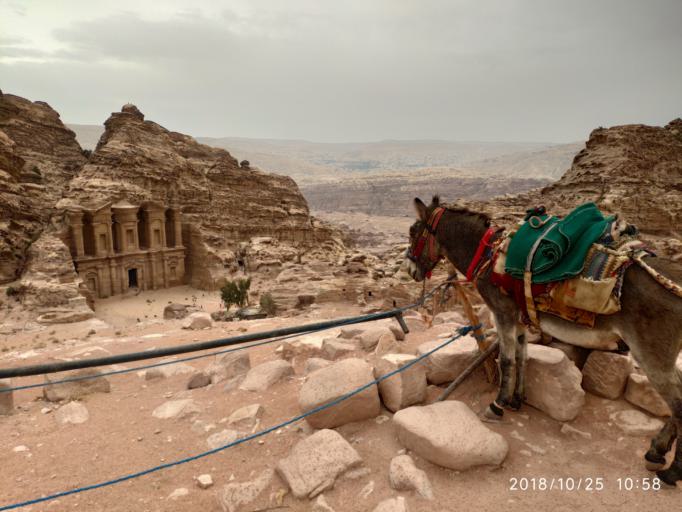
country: JO
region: Ma'an
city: Petra
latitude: 30.3380
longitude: 35.4286
